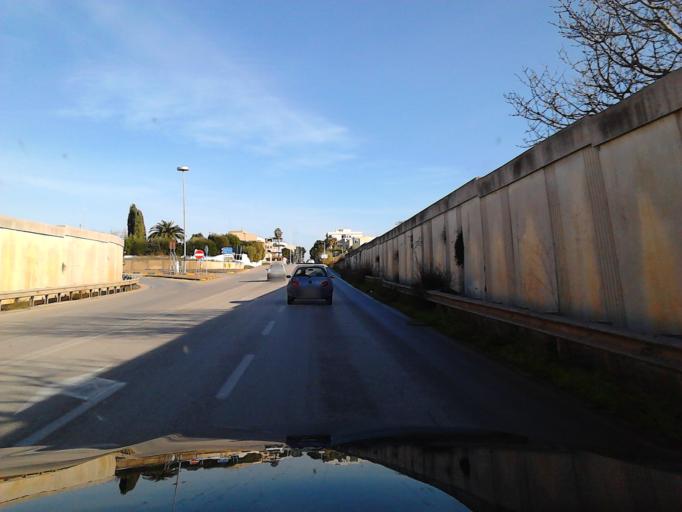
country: IT
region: Apulia
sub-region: Provincia di Bari
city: Rutigliano
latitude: 41.0075
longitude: 16.9919
